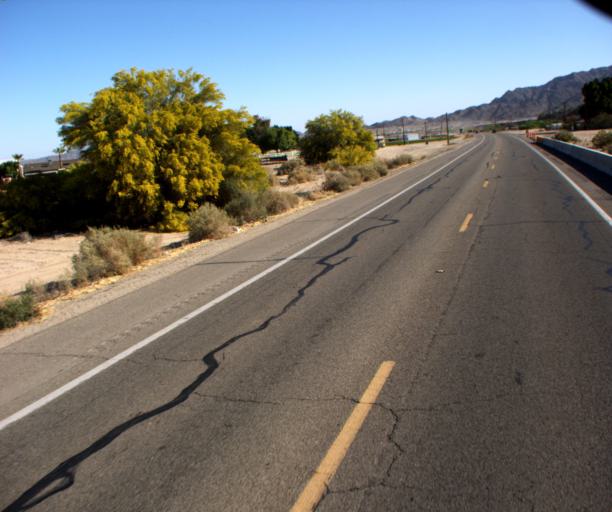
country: US
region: Arizona
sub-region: Yuma County
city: Fortuna Foothills
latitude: 32.7090
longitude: -114.4312
